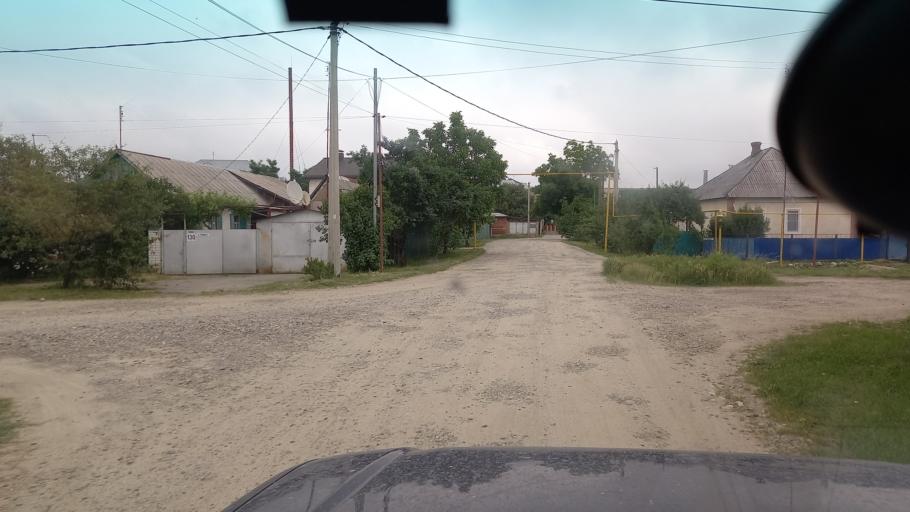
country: RU
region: Krasnodarskiy
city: Mostovskoy
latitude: 44.4125
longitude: 40.7890
